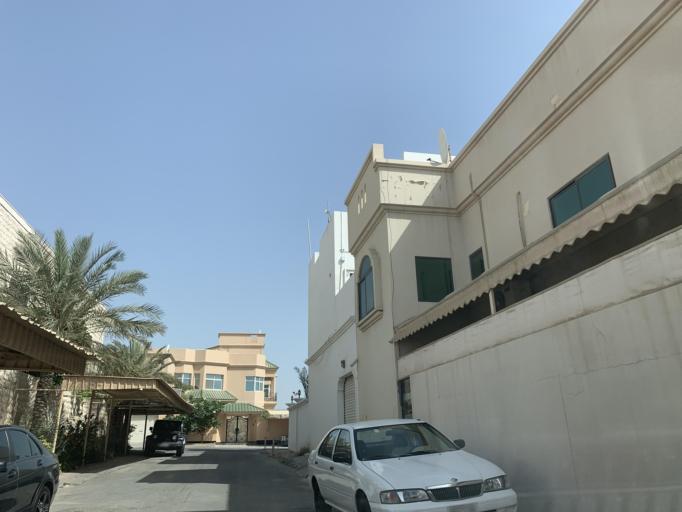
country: BH
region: Northern
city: Ar Rifa'
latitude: 26.1511
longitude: 50.5774
